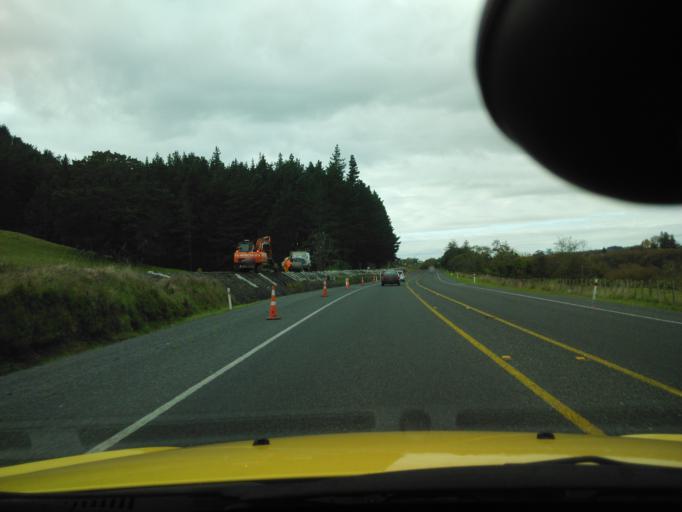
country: NZ
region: Waikato
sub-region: Waikato District
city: Ngaruawahia
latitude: -37.6047
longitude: 175.1762
